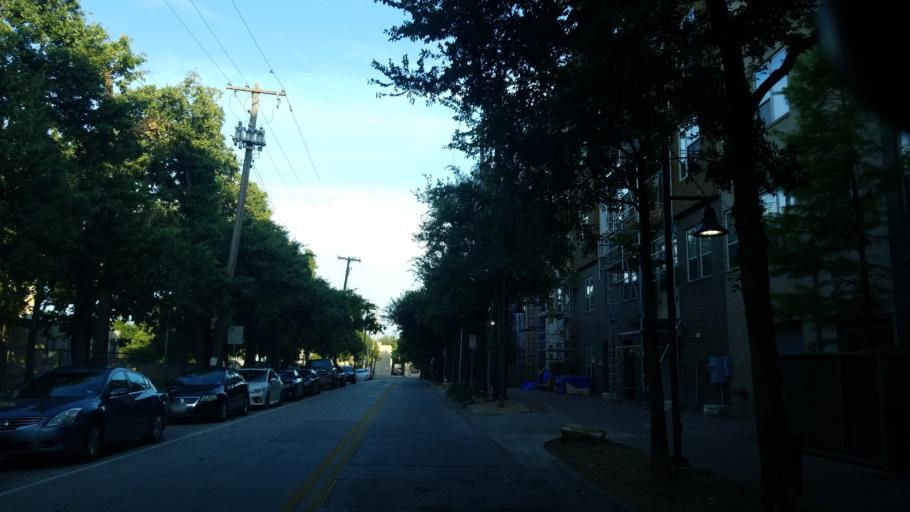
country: US
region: Texas
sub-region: Dallas County
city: Highland Park
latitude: 32.8076
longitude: -96.7896
